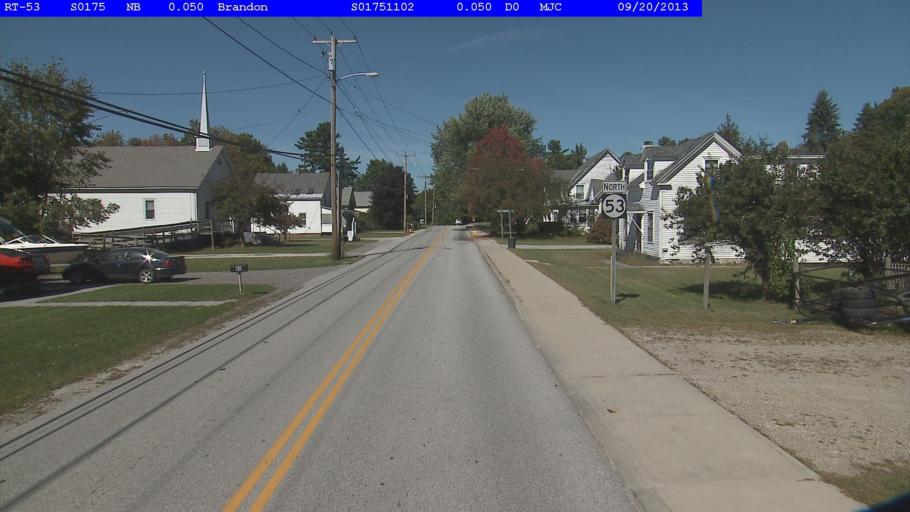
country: US
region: Vermont
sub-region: Rutland County
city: Brandon
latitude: 43.8279
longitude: -73.0535
